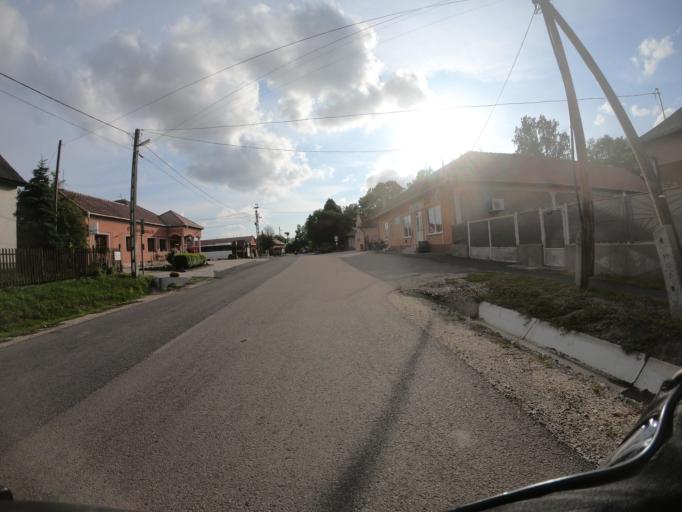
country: HU
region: Borsod-Abauj-Zemplen
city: Mezokeresztes
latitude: 47.8299
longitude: 20.7745
